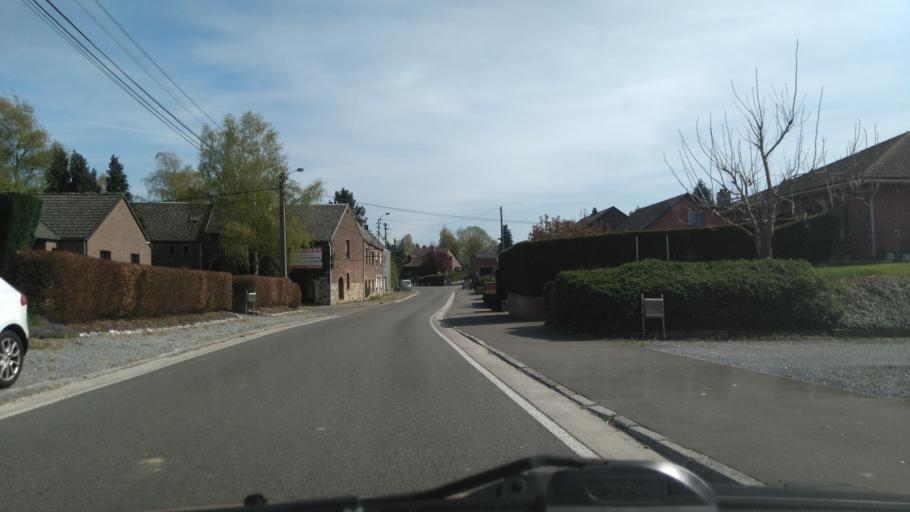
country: BE
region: Wallonia
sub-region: Province de Liege
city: Verlaine
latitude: 50.5904
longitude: 5.3453
